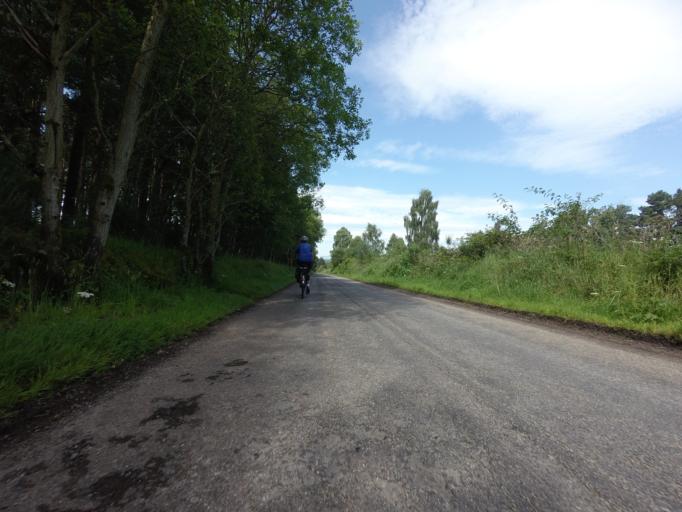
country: GB
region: Scotland
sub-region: Highland
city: Inverness
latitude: 57.5187
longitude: -4.2923
